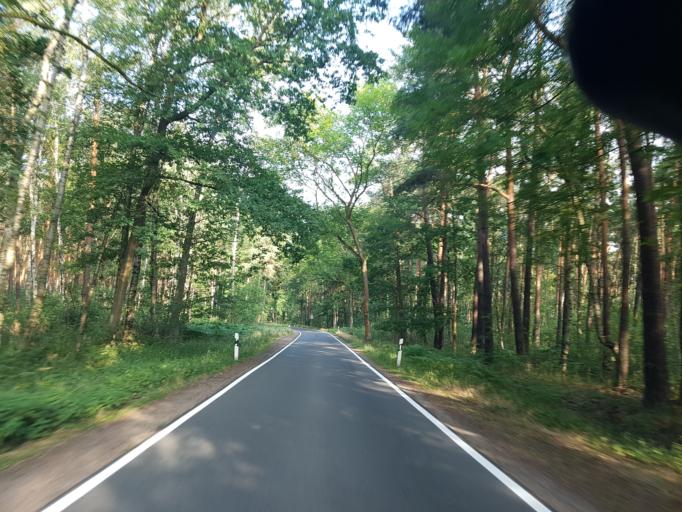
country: DE
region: Saxony-Anhalt
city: Holzdorf
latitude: 51.8549
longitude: 13.0802
